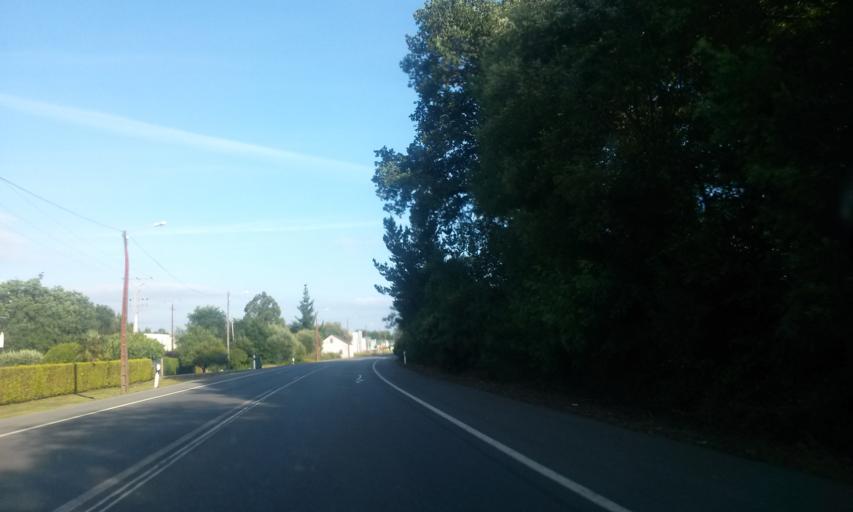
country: ES
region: Galicia
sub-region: Provincia de Lugo
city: Begonte
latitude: 43.1606
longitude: -7.6988
